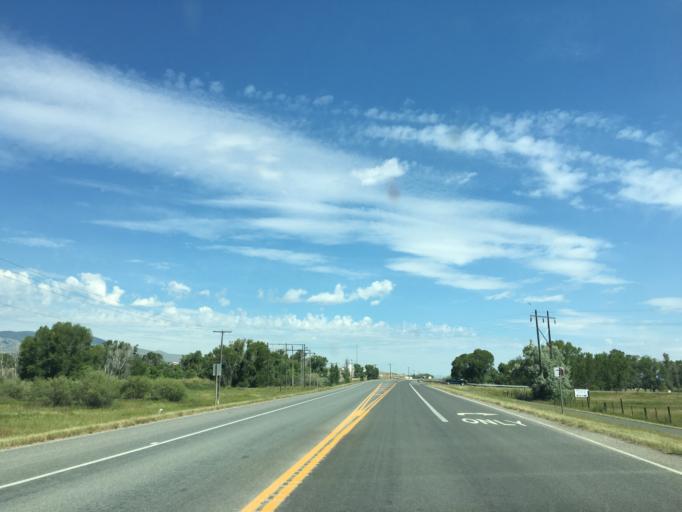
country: US
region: Montana
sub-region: Broadwater County
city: Townsend
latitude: 46.3309
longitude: -111.5292
